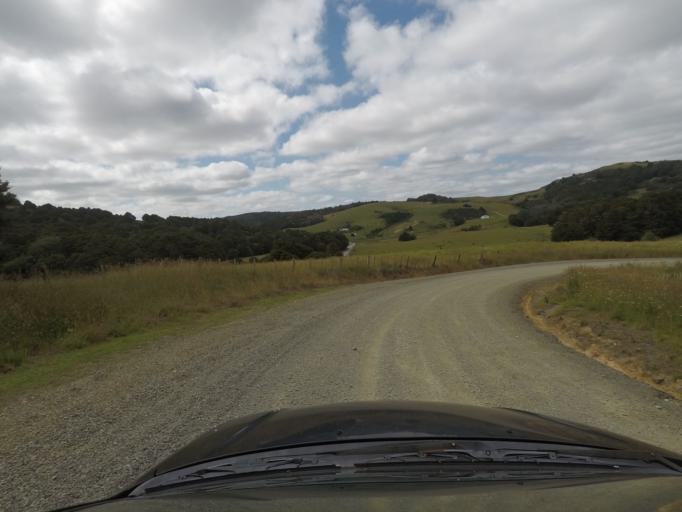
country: NZ
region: Northland
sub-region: Whangarei
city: Ruakaka
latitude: -35.9309
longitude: 174.3461
